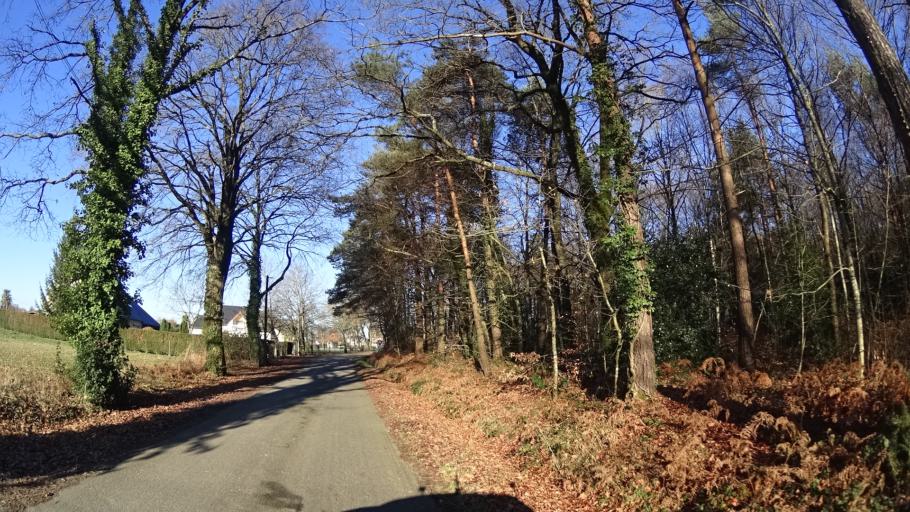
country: FR
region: Brittany
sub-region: Departement du Morbihan
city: Allaire
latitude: 47.6397
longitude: -2.1578
